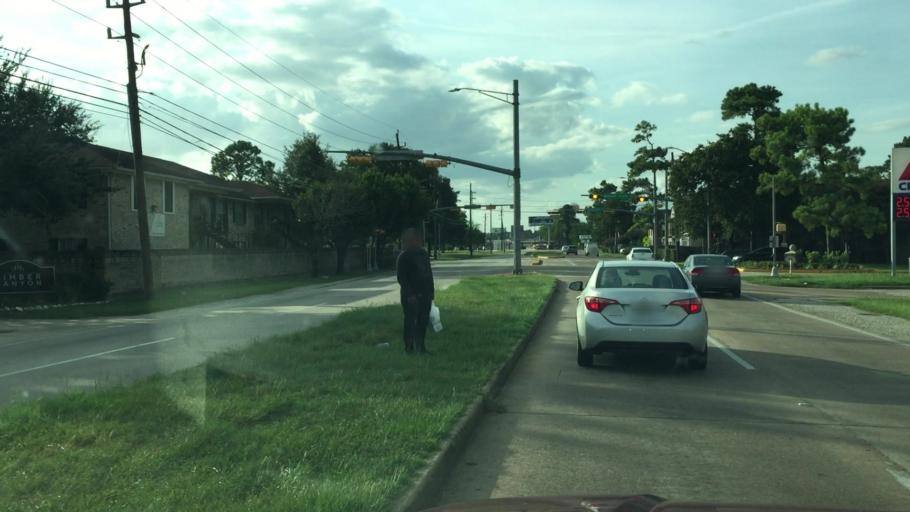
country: US
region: Texas
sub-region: Harris County
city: Hudson
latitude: 30.0159
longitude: -95.5187
